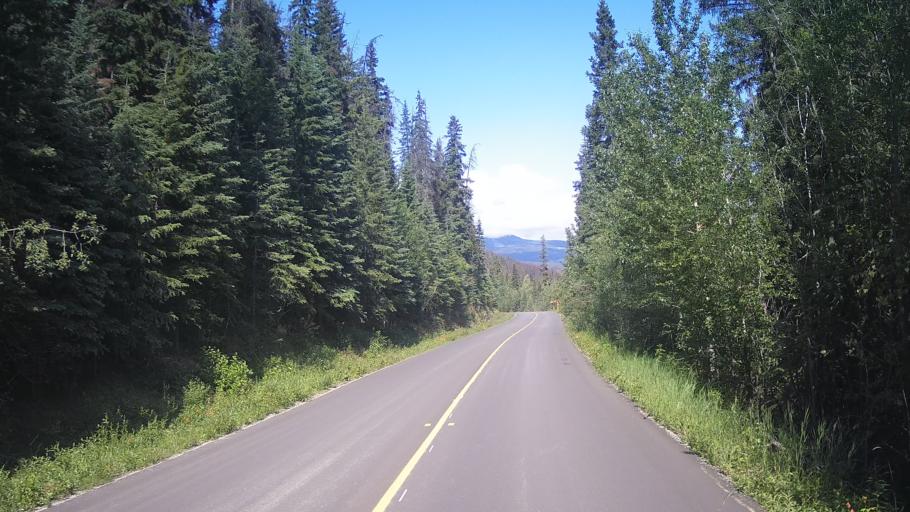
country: CA
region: Alberta
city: Jasper Park Lodge
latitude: 52.7405
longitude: -117.9623
